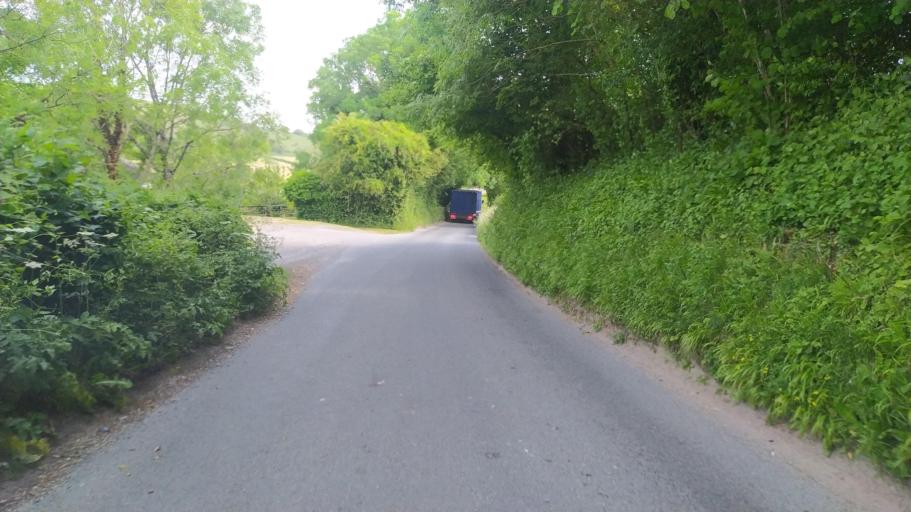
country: GB
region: England
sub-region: Dorset
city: Dorchester
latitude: 50.8060
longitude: -2.4898
